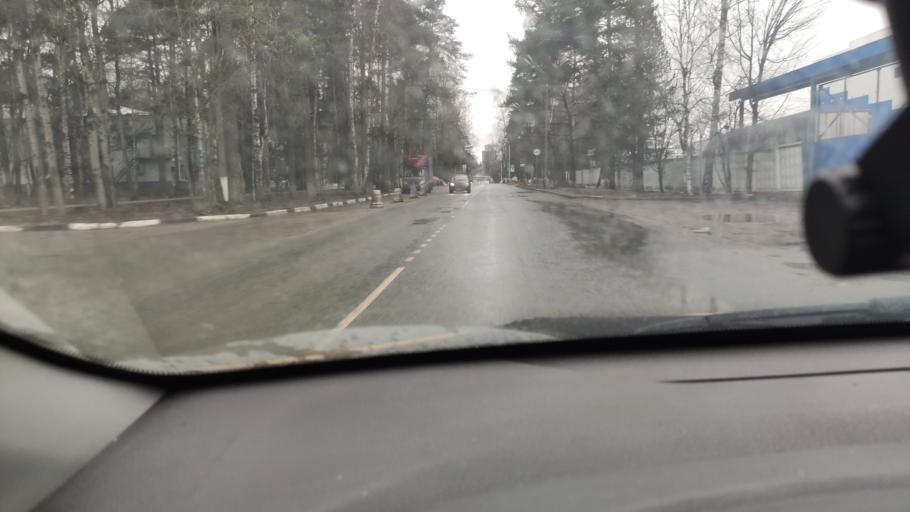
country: RU
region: Moskovskaya
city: Selyatino
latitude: 55.5181
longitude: 36.9772
